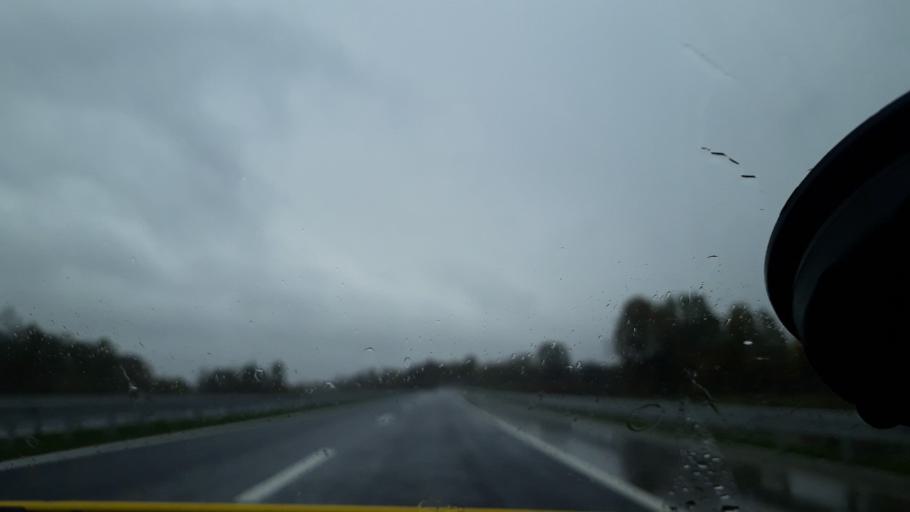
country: BA
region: Republika Srpska
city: Maglajani
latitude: 44.8900
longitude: 17.3703
